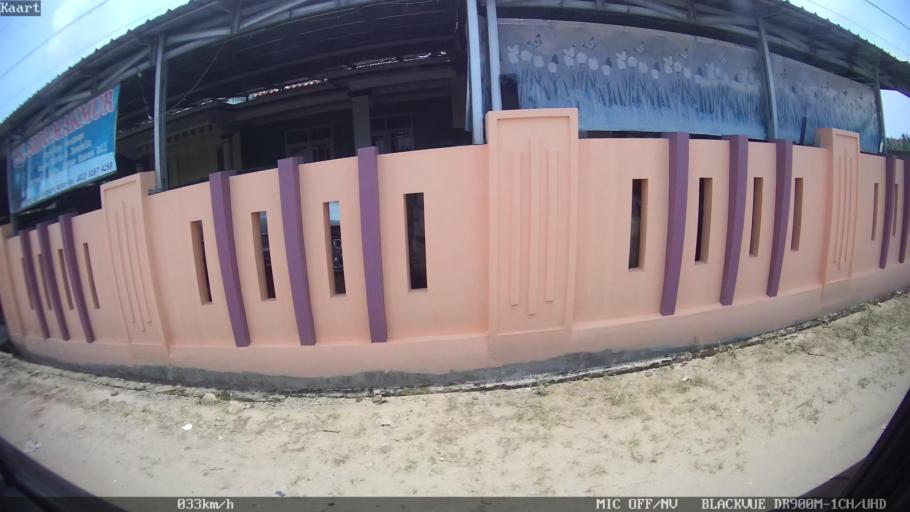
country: ID
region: Lampung
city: Kedaton
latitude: -5.3298
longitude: 105.2469
